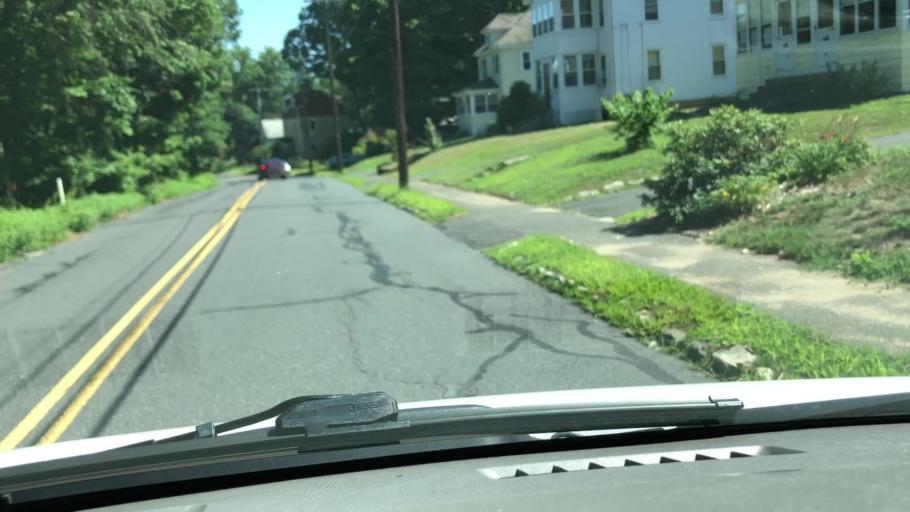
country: US
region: Massachusetts
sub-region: Hampshire County
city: Northampton
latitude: 42.3312
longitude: -72.6634
